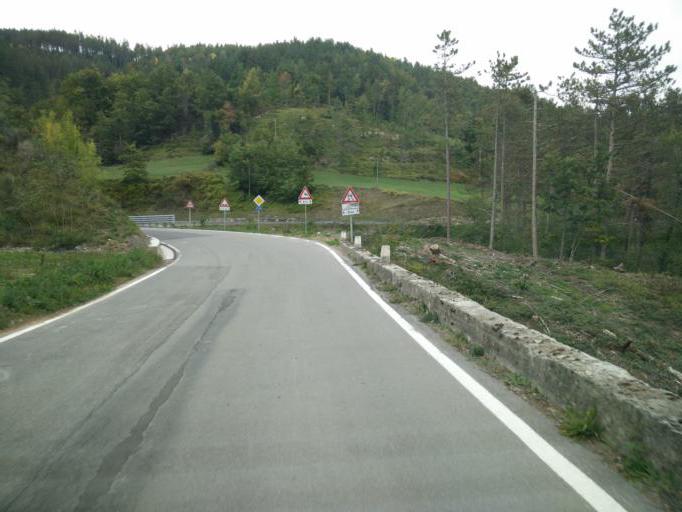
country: IT
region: Tuscany
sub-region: Provincia di Lucca
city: Giuncugnano
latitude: 44.2009
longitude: 10.2319
